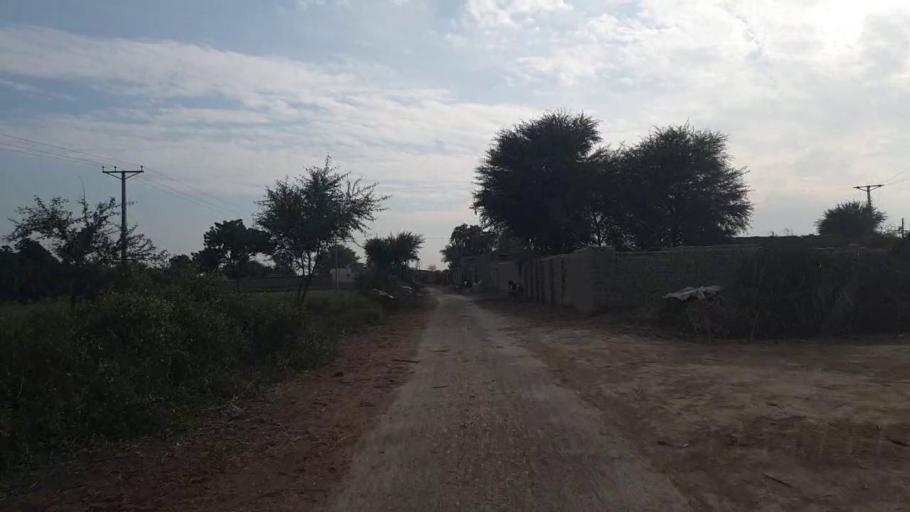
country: PK
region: Sindh
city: Shahdadpur
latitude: 26.0471
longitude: 68.5768
